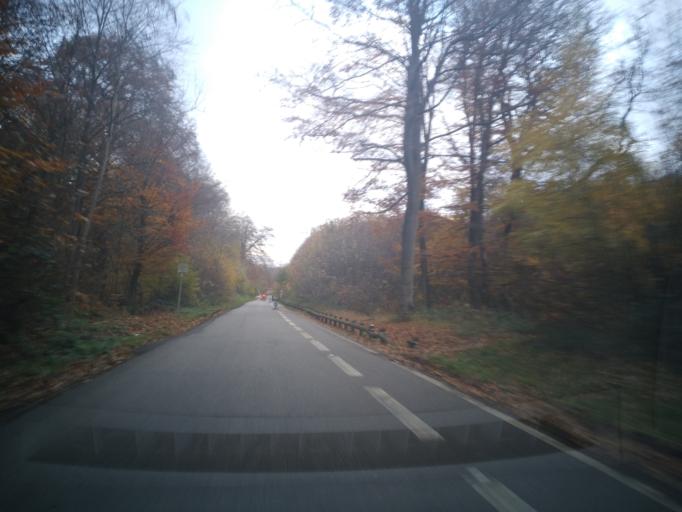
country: FR
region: Ile-de-France
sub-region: Departement des Yvelines
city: Saint-Nom-la-Breteche
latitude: 48.8653
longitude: 2.0439
